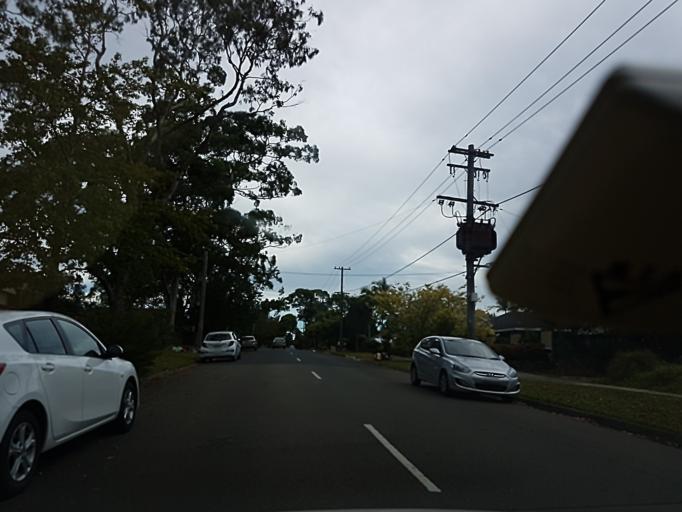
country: AU
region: New South Wales
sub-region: Warringah
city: Davidson
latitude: -33.7379
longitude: 151.2152
